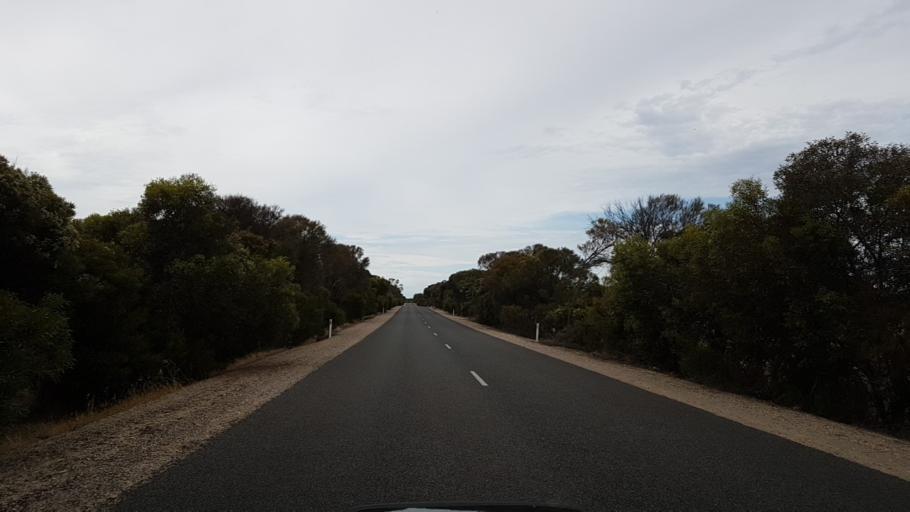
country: AU
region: South Australia
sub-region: Yorke Peninsula
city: Honiton
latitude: -34.9587
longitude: 137.1040
